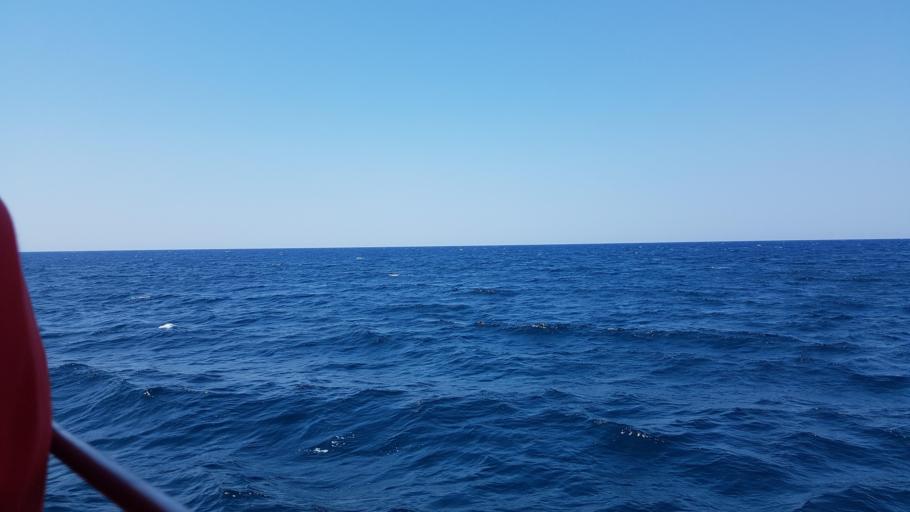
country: GR
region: Crete
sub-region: Nomos Chanias
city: Chania
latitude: 35.5214
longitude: 24.0149
